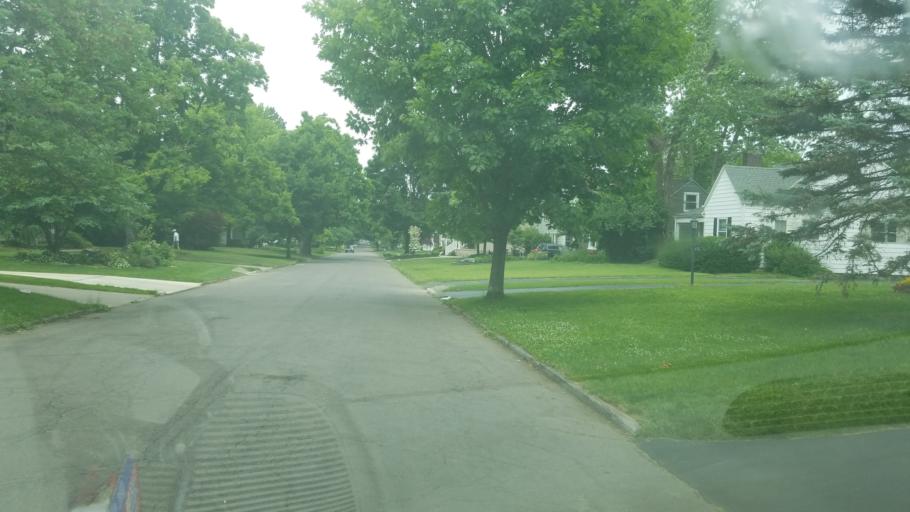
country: US
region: Ohio
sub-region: Franklin County
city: Worthington
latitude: 40.0571
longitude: -83.0067
